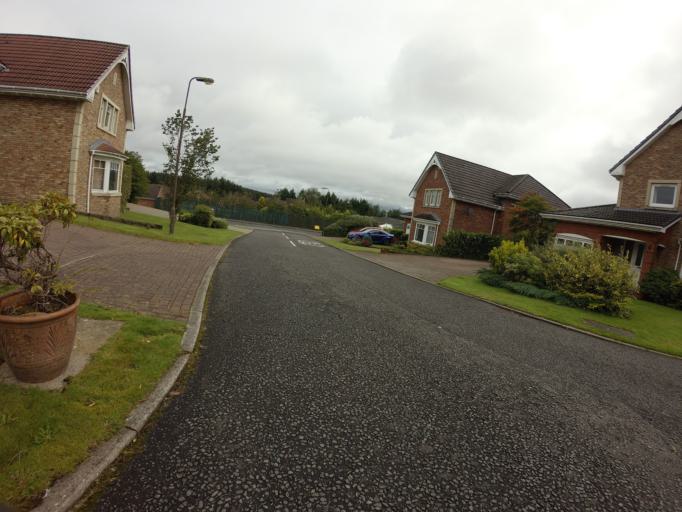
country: GB
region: Scotland
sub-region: West Lothian
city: Livingston
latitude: 55.9131
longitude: -3.5383
